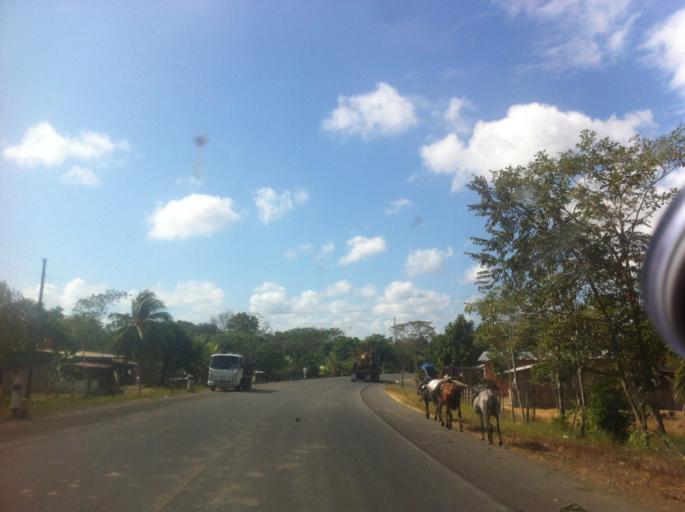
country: NI
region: Rio San Juan
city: San Carlos
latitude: 11.2324
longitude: -84.6896
